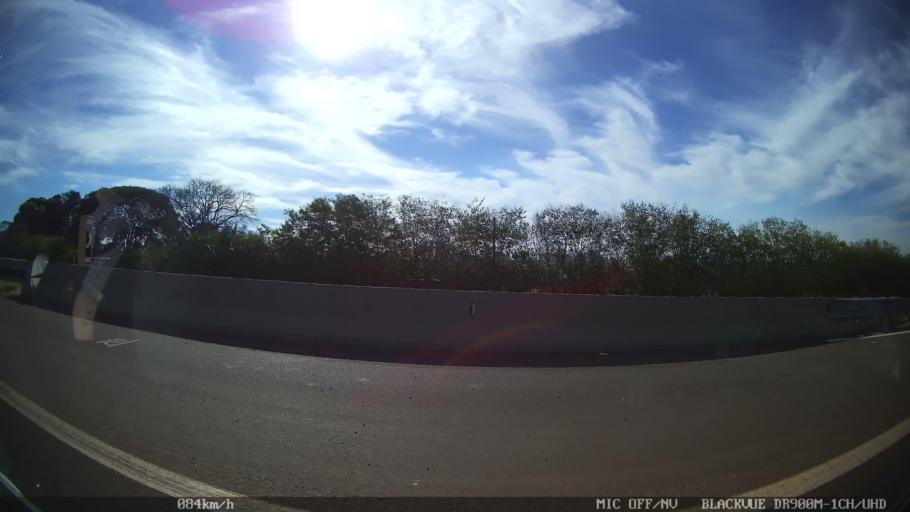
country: BR
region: Sao Paulo
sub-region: Araraquara
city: Araraquara
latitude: -21.8168
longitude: -48.1767
